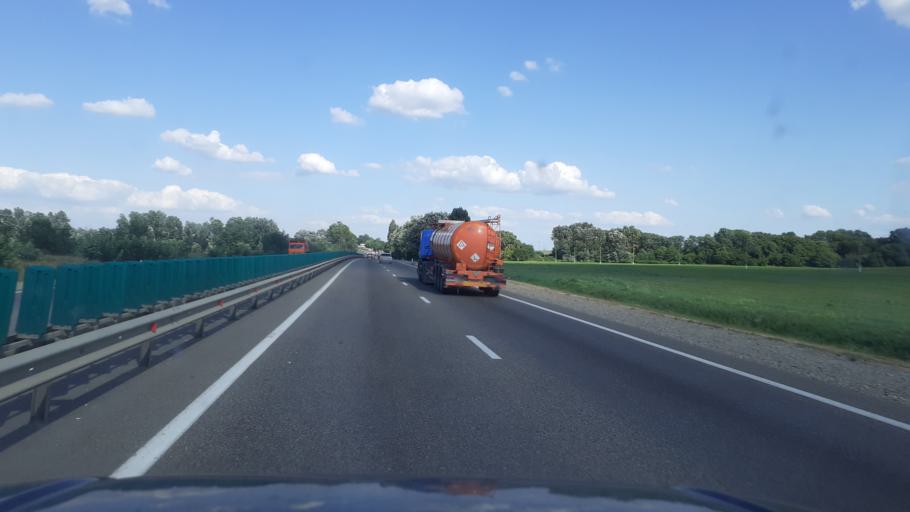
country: RU
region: Krasnodarskiy
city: Severskaya
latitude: 44.8544
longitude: 38.7307
